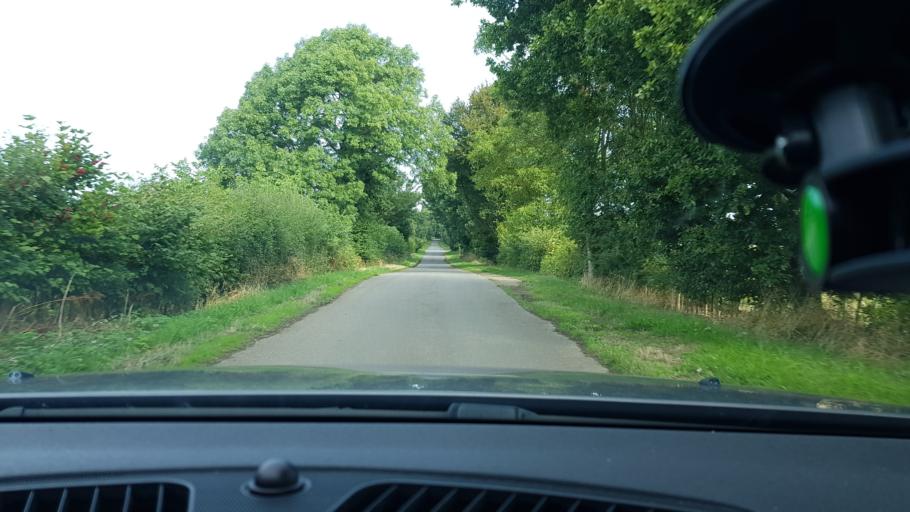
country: GB
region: England
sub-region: Wiltshire
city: Chilton Foliat
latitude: 51.4643
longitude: -1.5384
